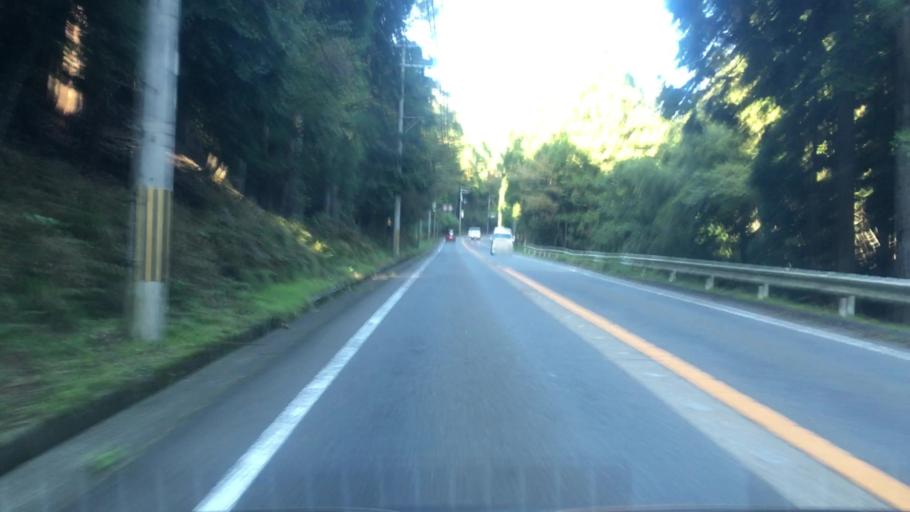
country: JP
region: Hyogo
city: Toyooka
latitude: 35.5791
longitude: 134.8562
